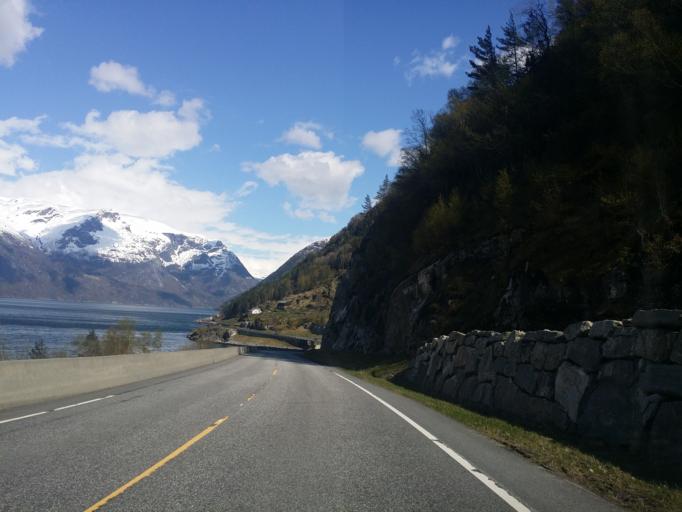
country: NO
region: Hordaland
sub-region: Ulvik
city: Ulvik
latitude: 60.4675
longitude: 6.8861
